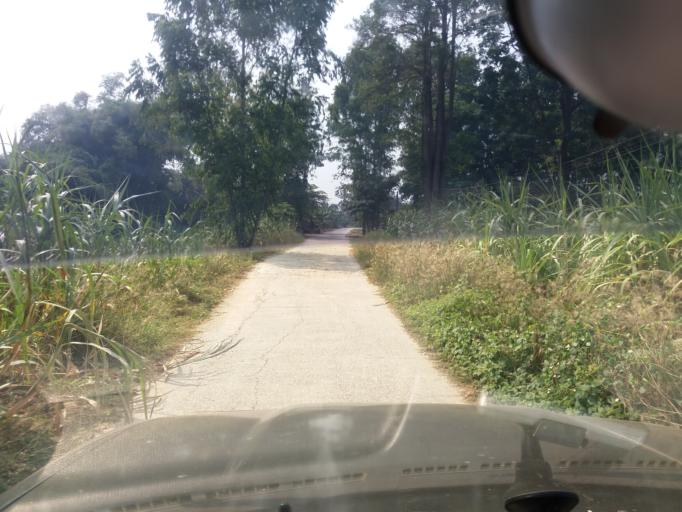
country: TH
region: Sing Buri
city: Bang Racham
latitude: 14.8997
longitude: 100.2165
